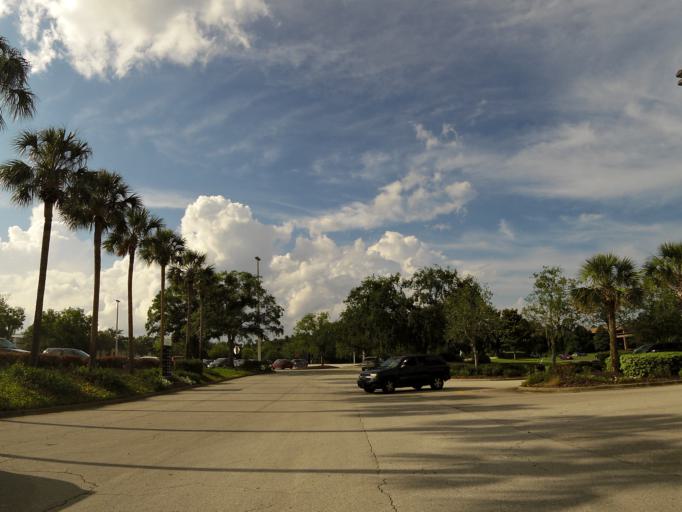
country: US
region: Florida
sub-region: Saint Johns County
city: Fruit Cove
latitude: 30.1850
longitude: -81.5526
